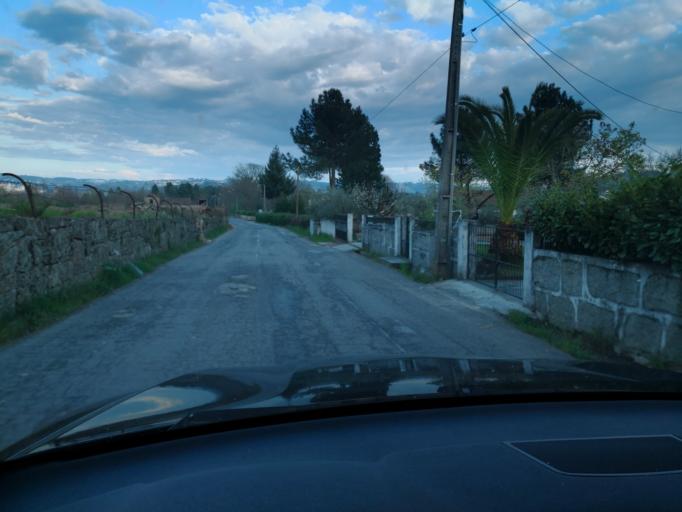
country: PT
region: Vila Real
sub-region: Vila Real
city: Vila Real
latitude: 41.2996
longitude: -7.7726
